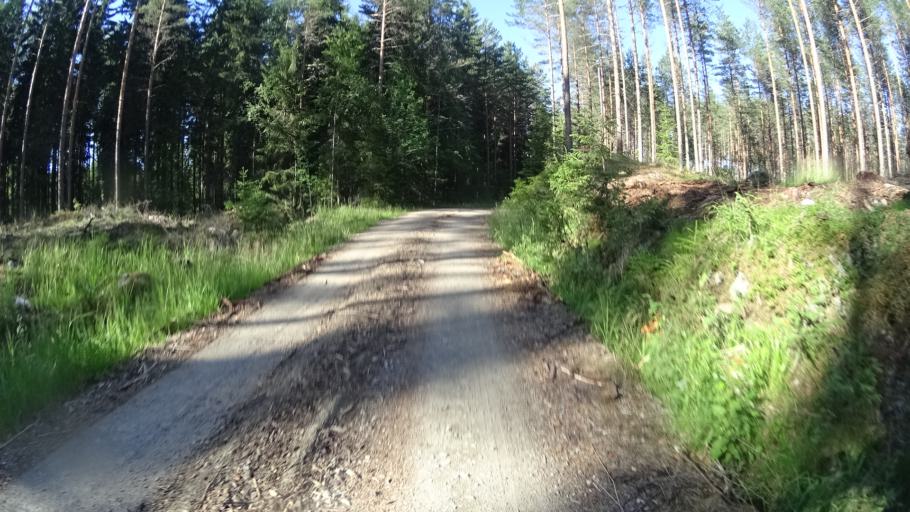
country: FI
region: Uusimaa
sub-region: Helsinki
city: Karkkila
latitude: 60.6438
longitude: 24.1652
